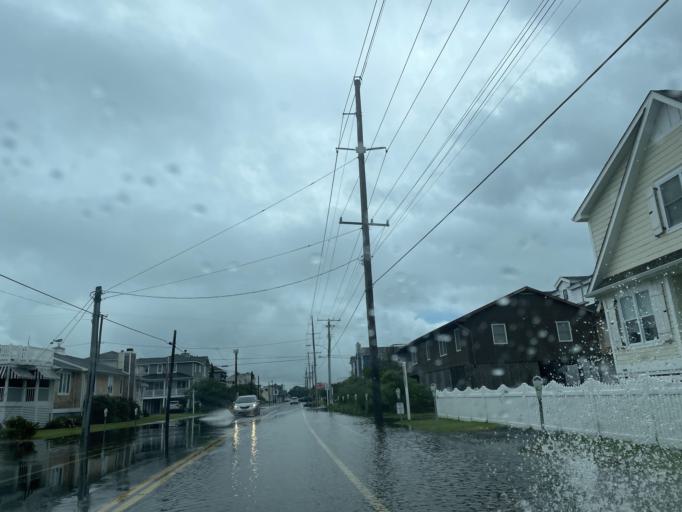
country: US
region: Delaware
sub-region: Sussex County
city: Bethany Beach
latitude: 38.5434
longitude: -75.0578
